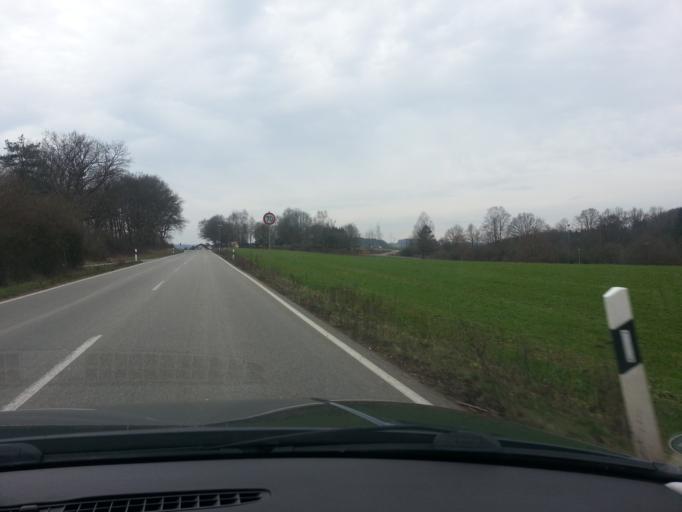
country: DE
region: Rheinland-Pfalz
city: Gries
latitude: 49.4100
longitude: 7.4036
